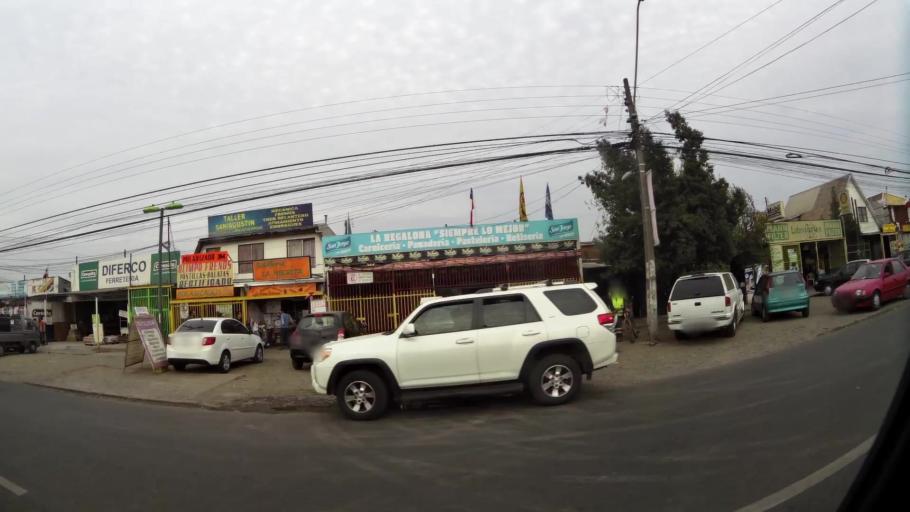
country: CL
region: Santiago Metropolitan
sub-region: Provincia de Santiago
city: Lo Prado
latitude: -33.5124
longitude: -70.7754
